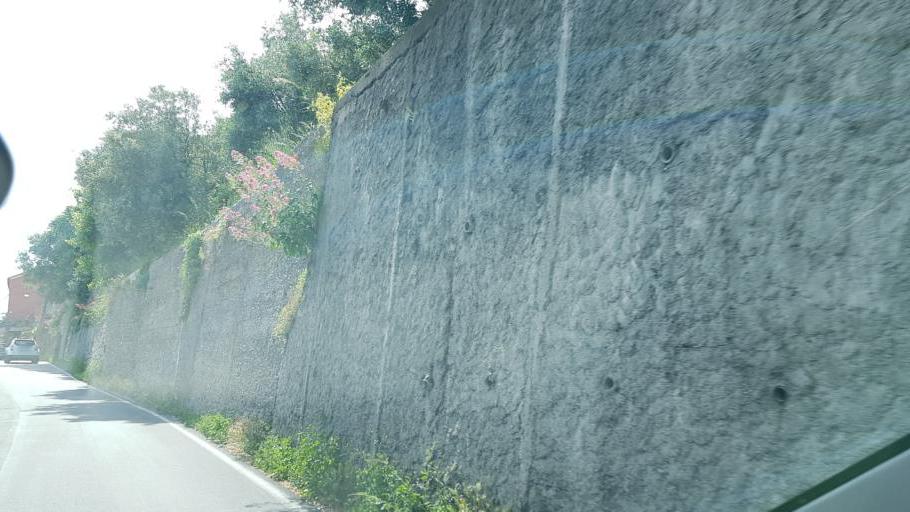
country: IT
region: Liguria
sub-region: Provincia di Genova
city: Bogliasco
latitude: 44.4038
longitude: 8.9940
